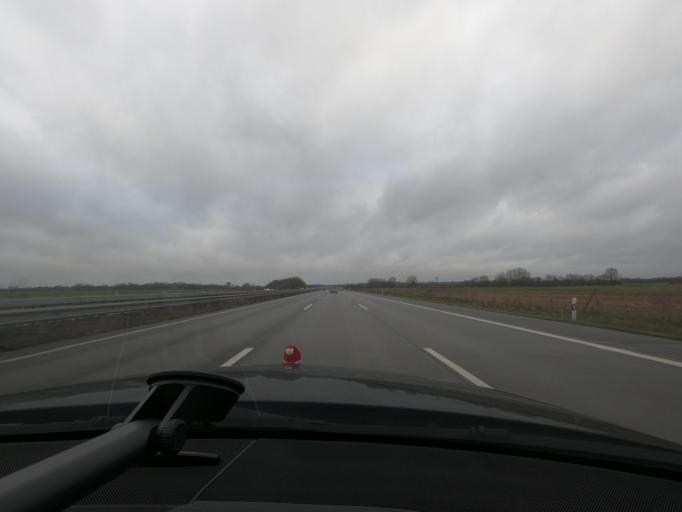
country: DE
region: Schleswig-Holstein
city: Loop
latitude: 54.1521
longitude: 9.9645
